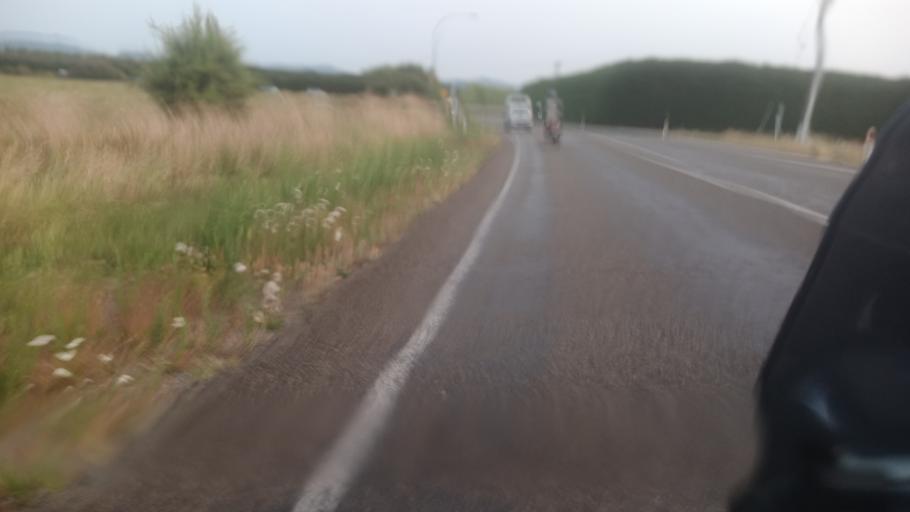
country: NZ
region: Bay of Plenty
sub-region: Opotiki District
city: Opotiki
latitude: -37.9986
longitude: 177.2982
